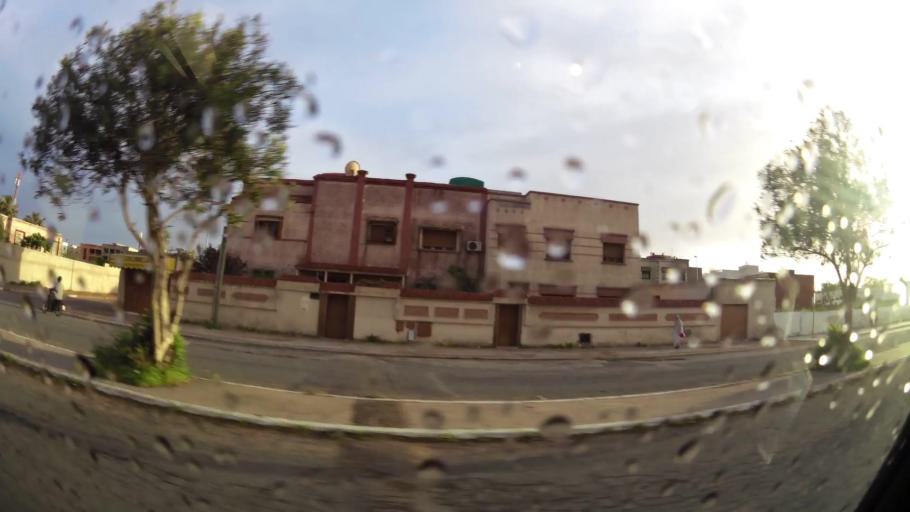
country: MA
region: Doukkala-Abda
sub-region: El-Jadida
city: El Jadida
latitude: 33.2391
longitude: -8.4899
